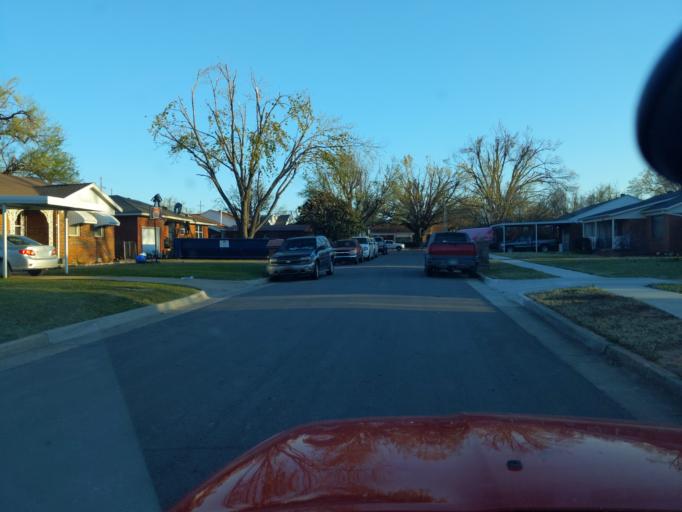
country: US
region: Oklahoma
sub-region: Oklahoma County
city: Oklahoma City
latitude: 35.4148
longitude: -97.5225
